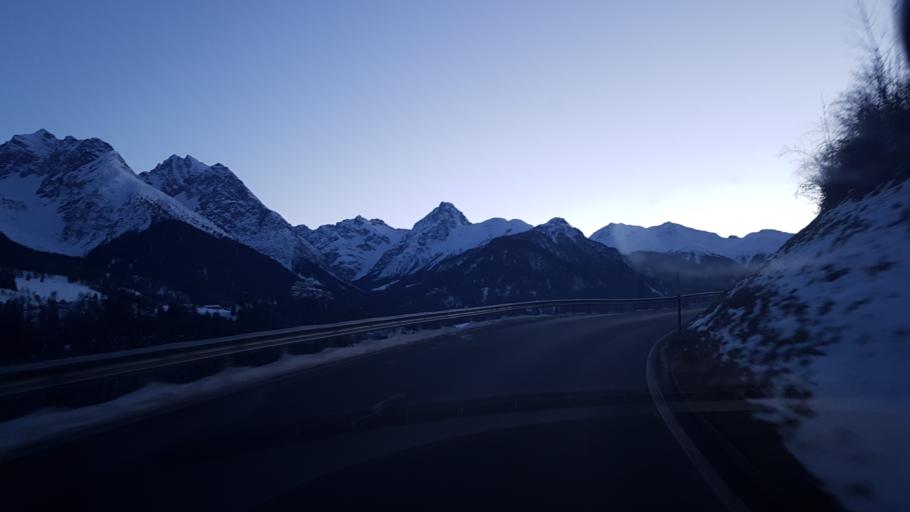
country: CH
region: Grisons
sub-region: Inn District
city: Scuol
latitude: 46.7922
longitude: 10.2692
